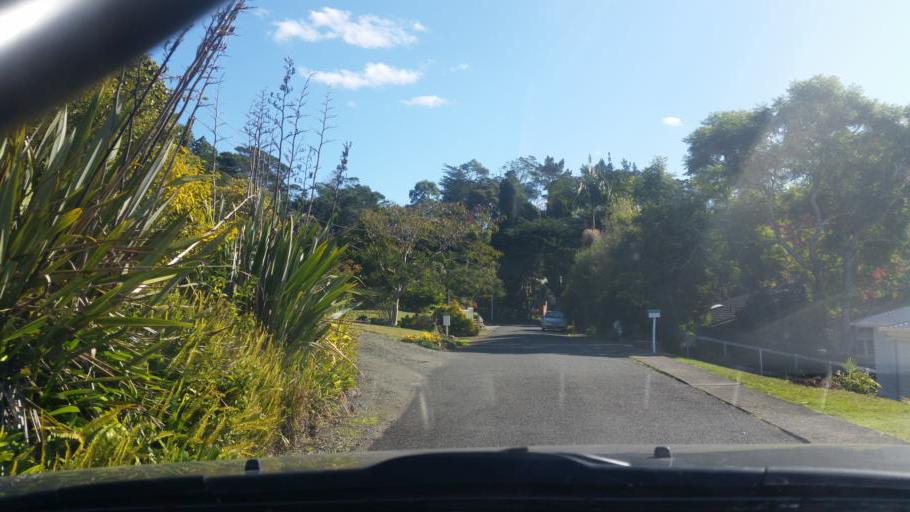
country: NZ
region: Northland
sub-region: Kaipara District
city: Dargaville
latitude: -35.9579
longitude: 173.8640
